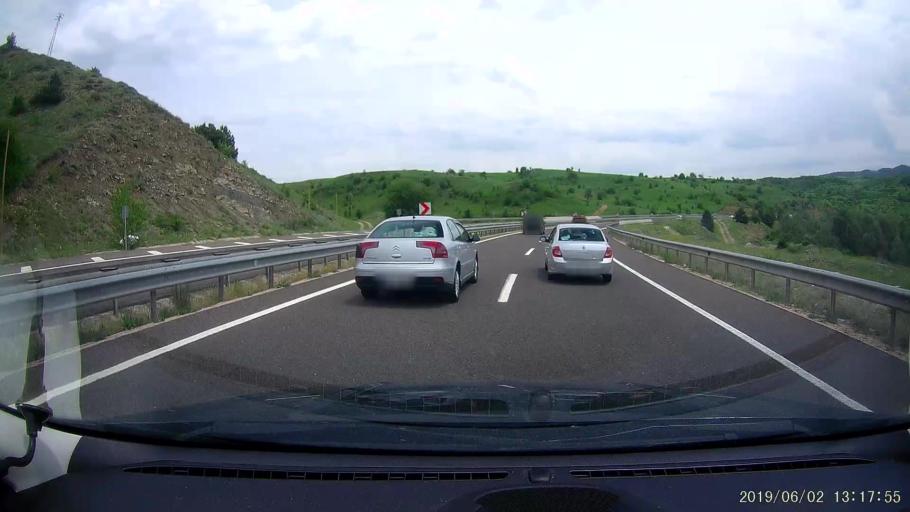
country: TR
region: Karabuk
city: Gozyeri
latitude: 40.8383
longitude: 32.7124
